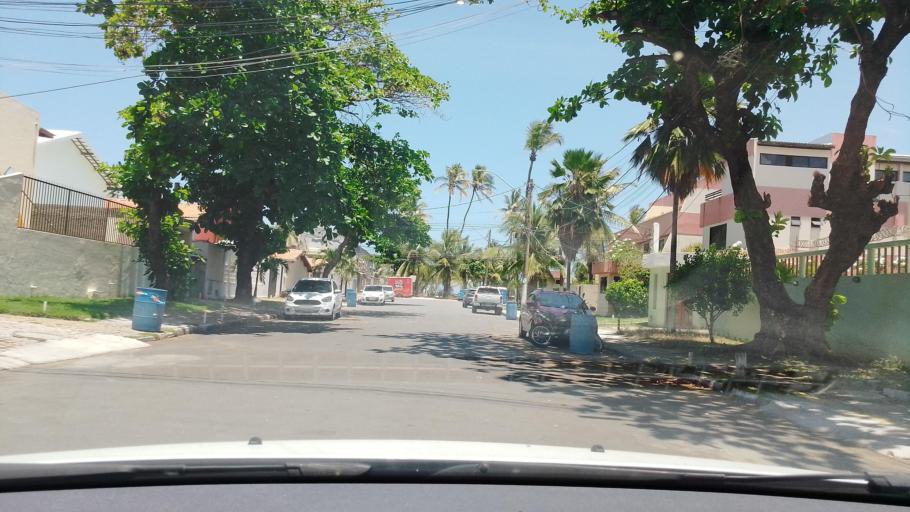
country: BR
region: Bahia
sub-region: Lauro De Freitas
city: Lauro de Freitas
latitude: -12.9335
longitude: -38.3260
